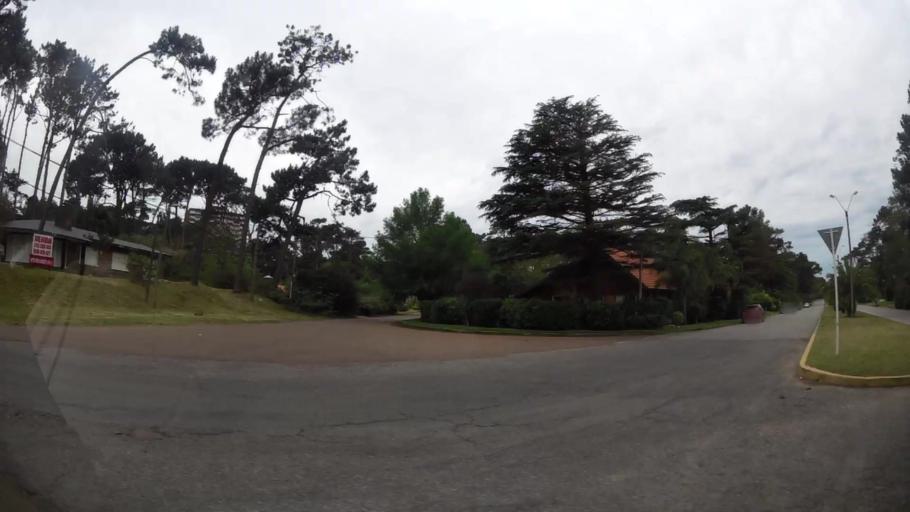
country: UY
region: Maldonado
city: Maldonado
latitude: -34.9279
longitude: -54.9560
